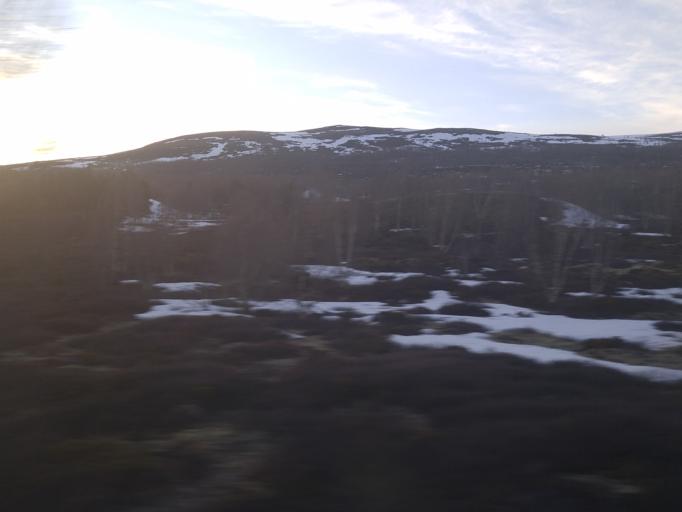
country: NO
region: Oppland
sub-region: Dovre
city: Dovre
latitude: 62.1708
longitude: 9.3699
